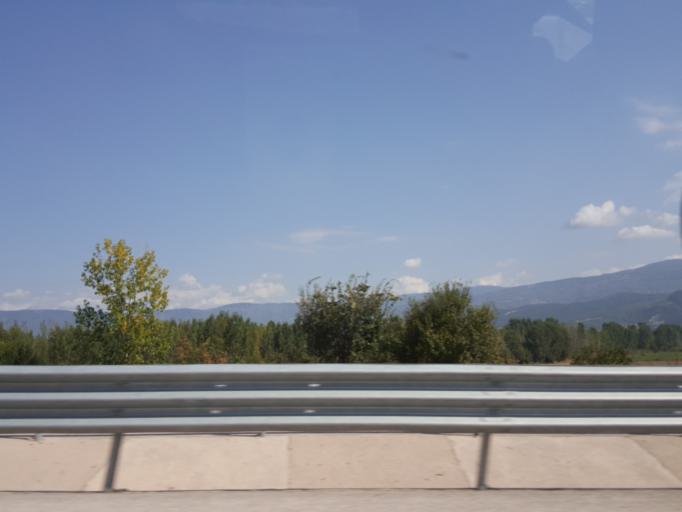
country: TR
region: Tokat
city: Niksar
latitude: 40.5197
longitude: 36.9092
